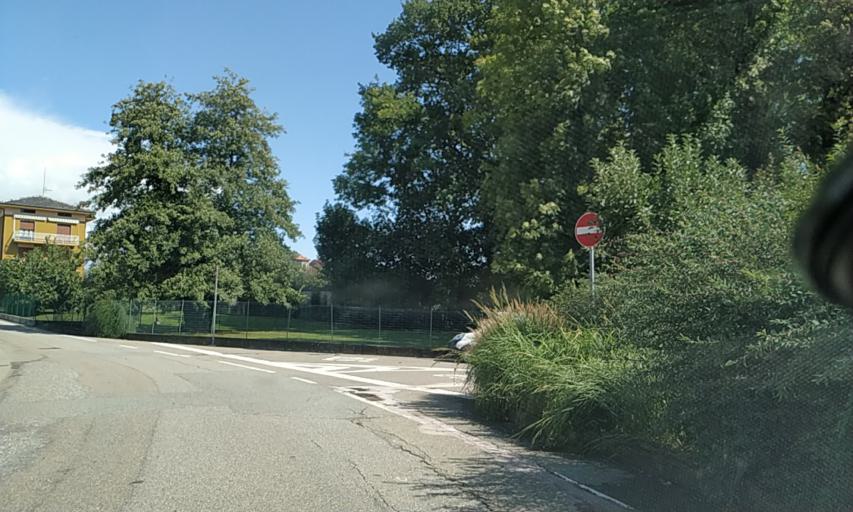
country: IT
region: Piedmont
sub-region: Provincia di Biella
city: Mongrando
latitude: 45.5266
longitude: 8.0080
